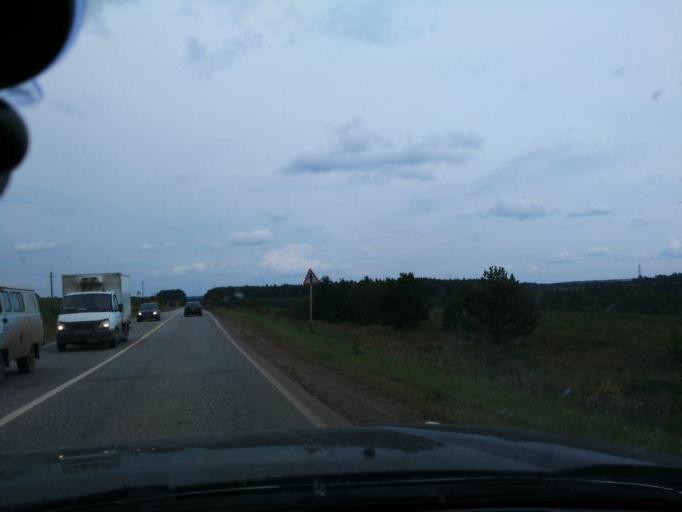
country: RU
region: Perm
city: Kuyeda
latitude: 56.4722
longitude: 55.7469
